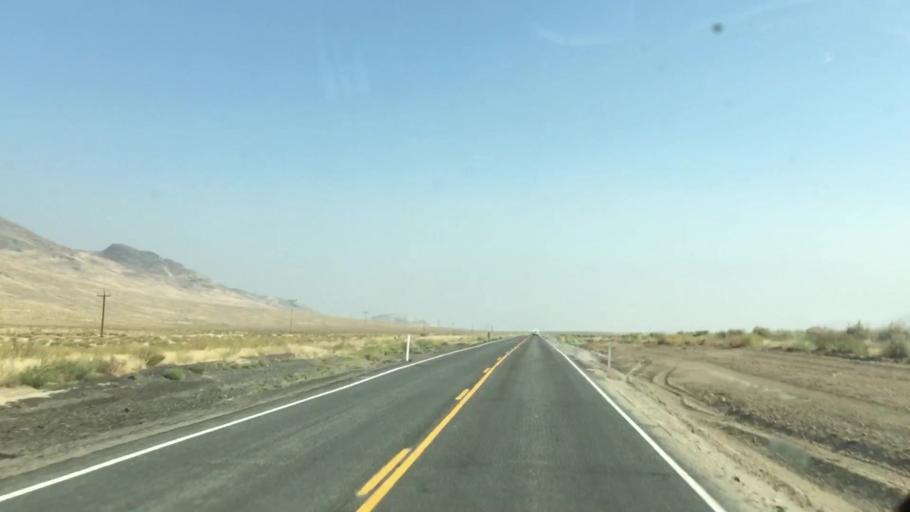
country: US
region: Nevada
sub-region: Lyon County
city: Fernley
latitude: 40.4065
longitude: -119.3337
